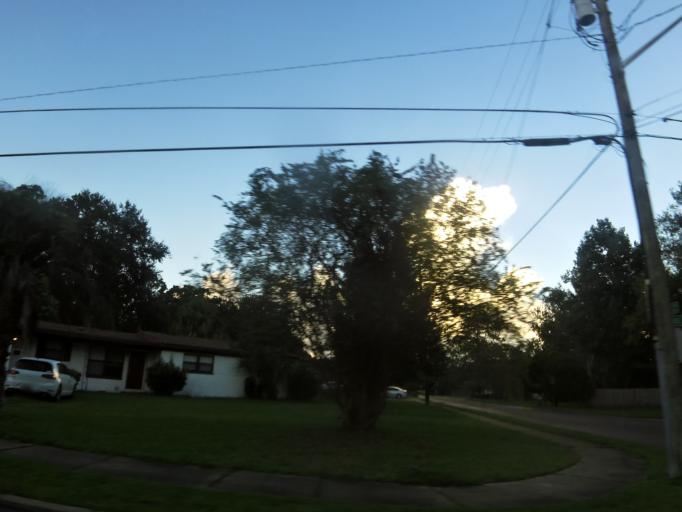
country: US
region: Florida
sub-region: Duval County
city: Jacksonville
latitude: 30.2337
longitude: -81.6146
